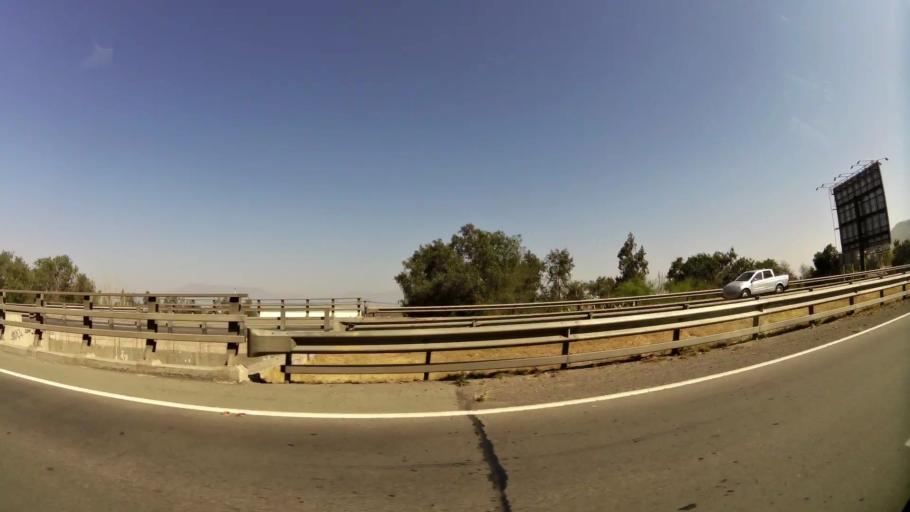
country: CL
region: Santiago Metropolitan
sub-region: Provincia de Chacabuco
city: Chicureo Abajo
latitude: -33.3425
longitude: -70.6942
